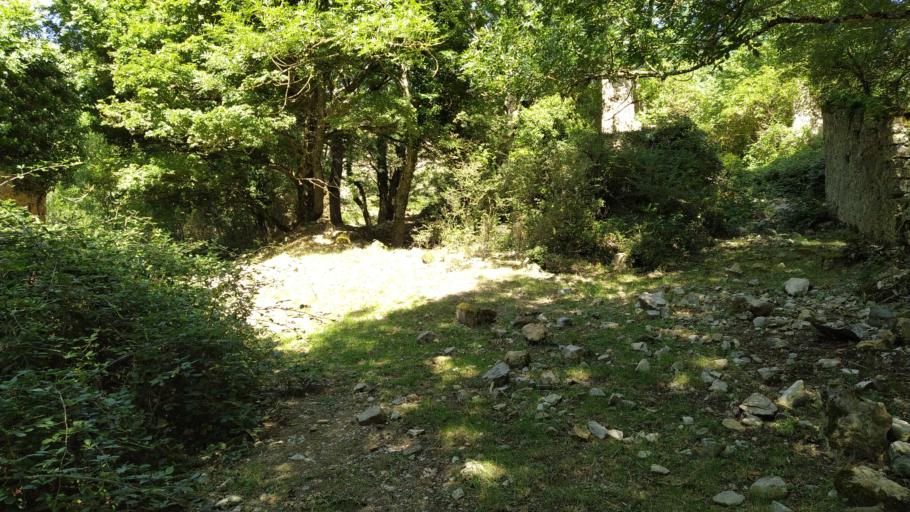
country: FR
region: Languedoc-Roussillon
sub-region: Departement des Pyrenees-Orientales
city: Saint-Paul-de-Fenouillet
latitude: 42.8512
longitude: 2.3898
